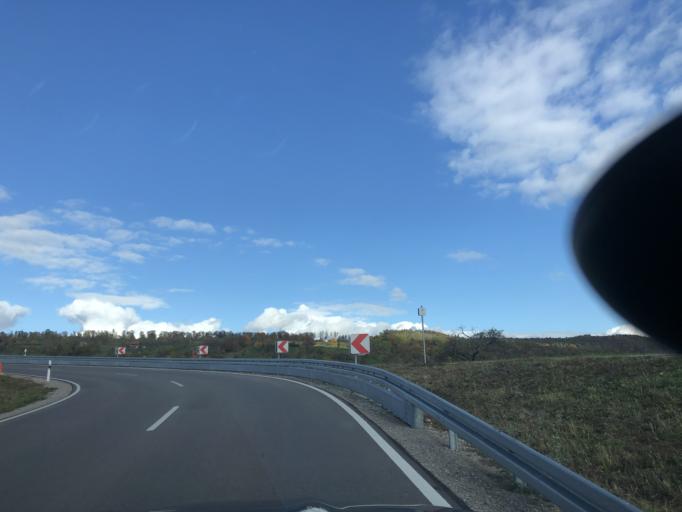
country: DE
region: Baden-Wuerttemberg
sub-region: Regierungsbezirk Stuttgart
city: Allmersbach im Tal
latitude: 48.8812
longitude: 9.4689
